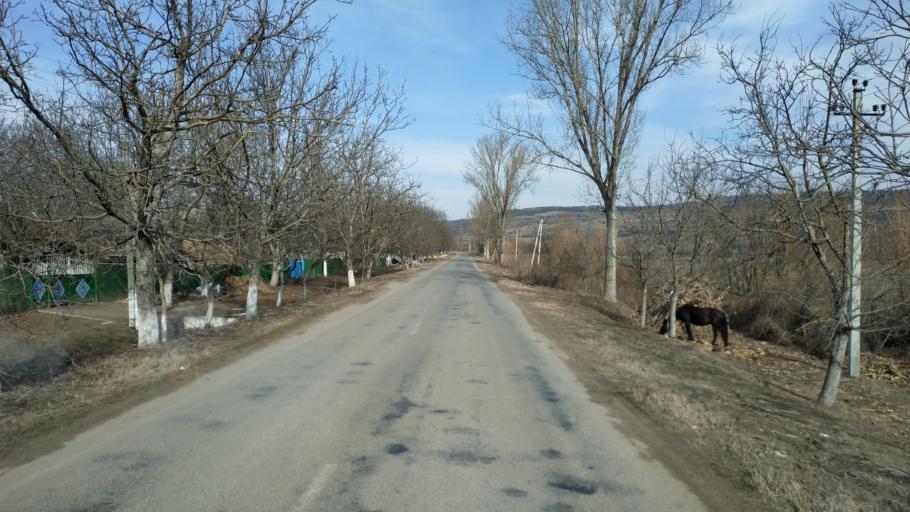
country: MD
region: Nisporeni
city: Nisporeni
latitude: 47.1501
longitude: 28.1078
